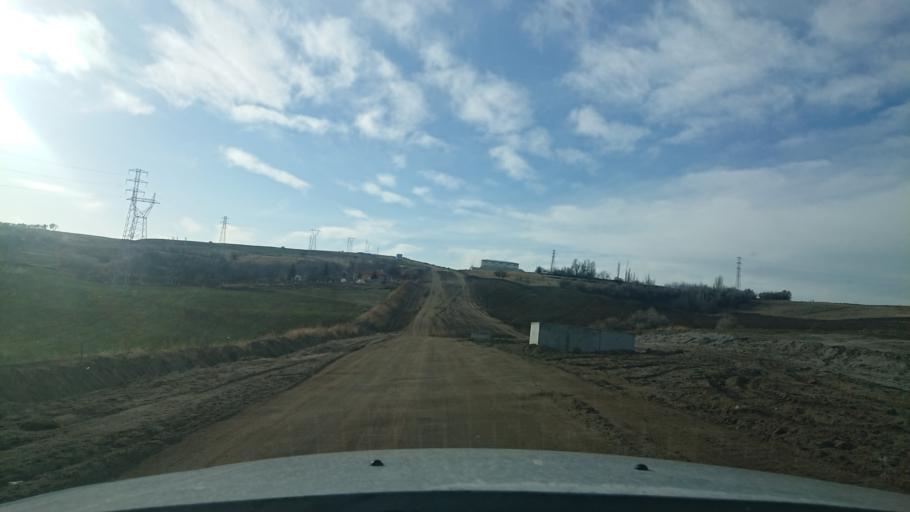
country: TR
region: Aksaray
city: Agacoren
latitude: 38.8578
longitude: 33.9429
